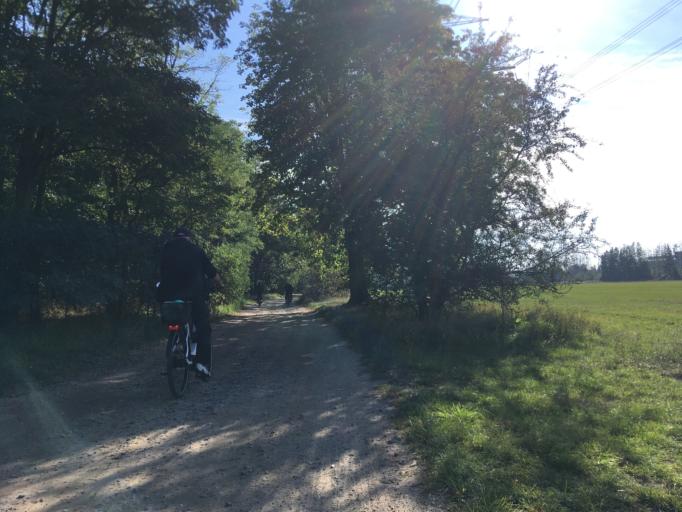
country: DE
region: Brandenburg
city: Altlandsberg
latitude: 52.5433
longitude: 13.7231
